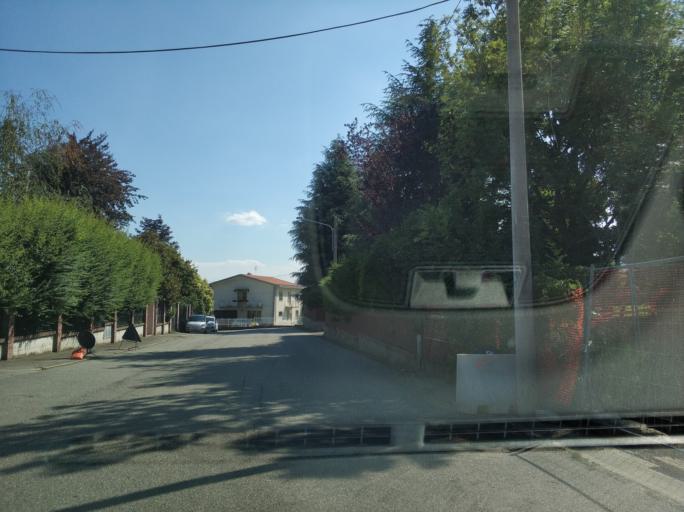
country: IT
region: Piedmont
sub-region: Provincia di Torino
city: San Carlo Canavese
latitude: 45.2466
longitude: 7.6039
